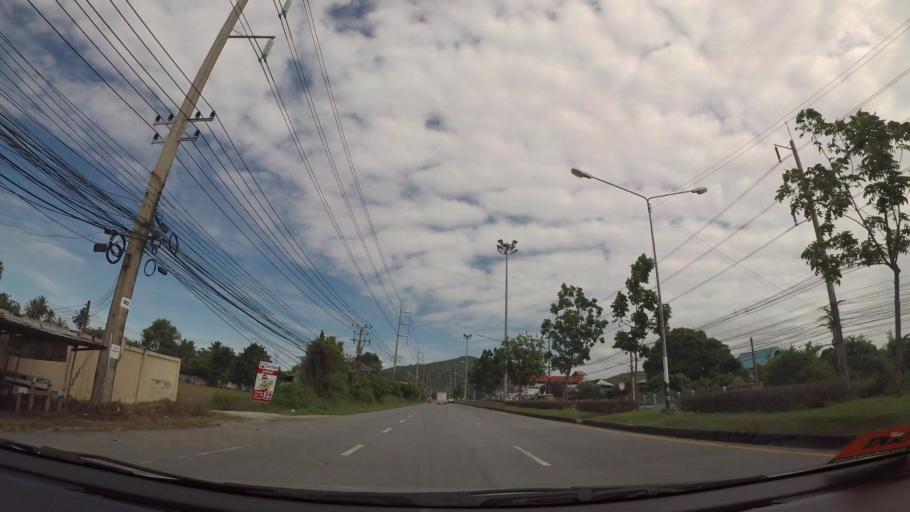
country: TH
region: Rayong
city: Ban Chang
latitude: 12.7455
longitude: 101.1131
